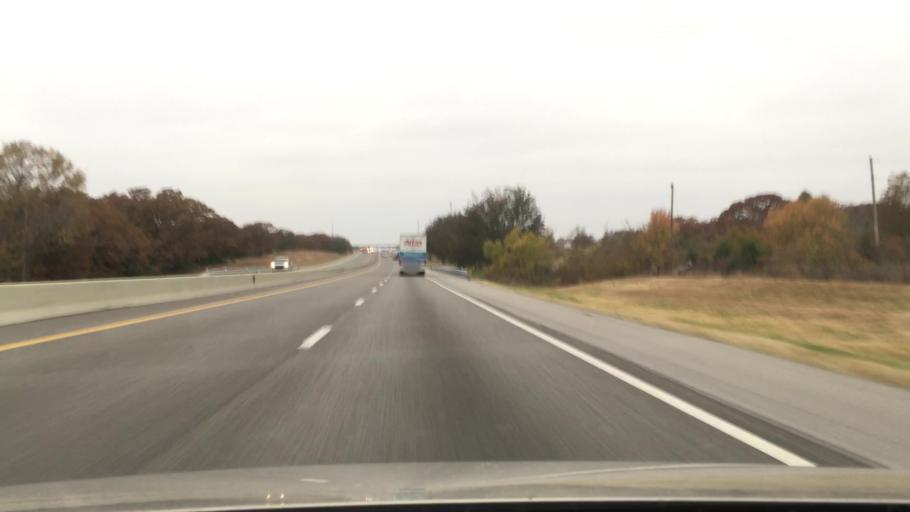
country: US
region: Oklahoma
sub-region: Lincoln County
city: Chandler
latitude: 35.7244
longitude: -96.8573
